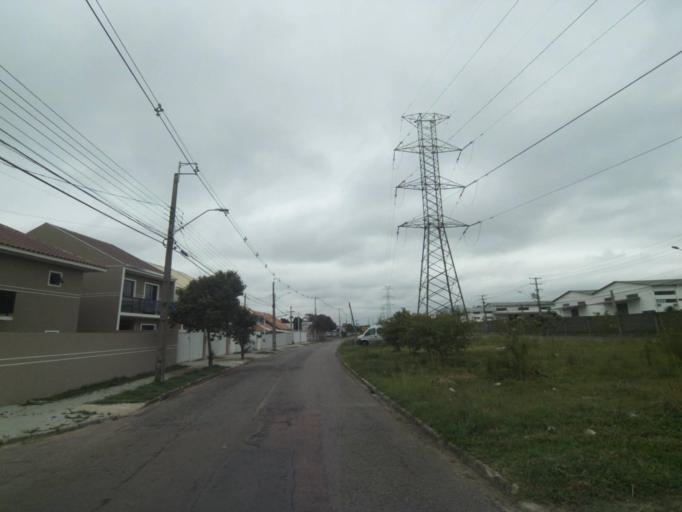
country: BR
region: Parana
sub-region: Araucaria
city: Araucaria
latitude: -25.5421
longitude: -49.3372
